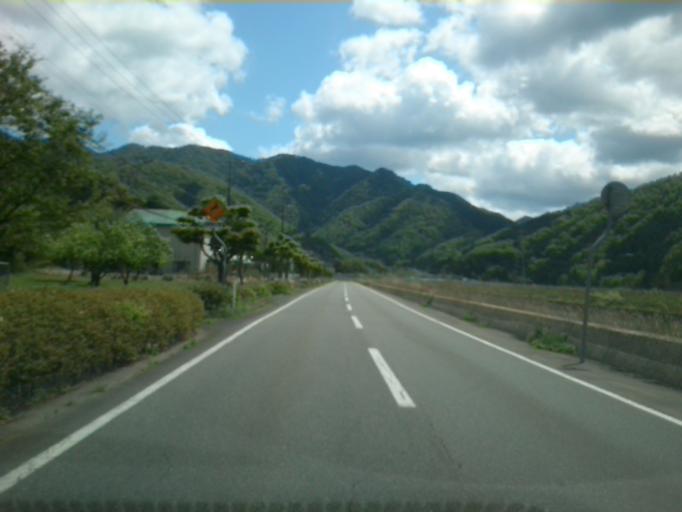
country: JP
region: Hyogo
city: Toyooka
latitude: 35.4538
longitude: 134.8718
